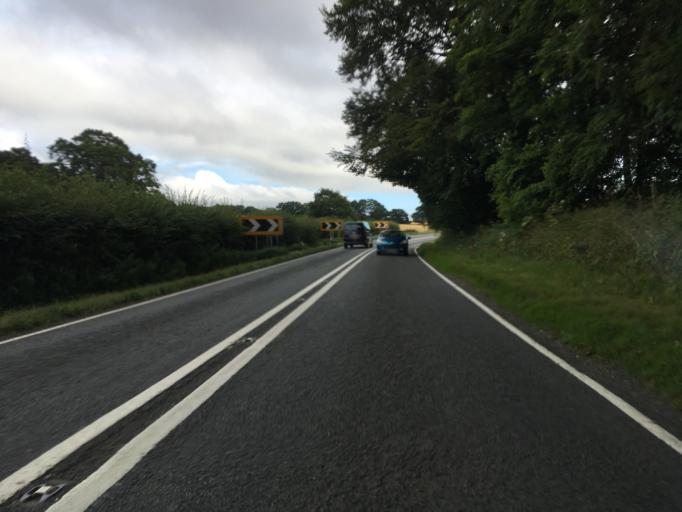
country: GB
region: England
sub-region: Hampshire
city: Four Marks
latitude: 51.0267
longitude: -1.0279
